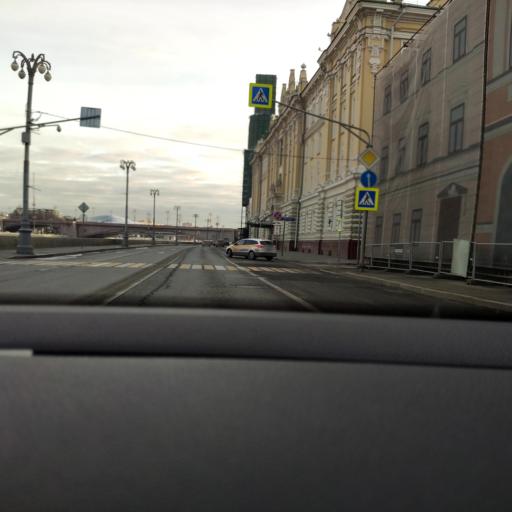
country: RU
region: Moscow
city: Moscow
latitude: 55.7477
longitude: 37.6198
